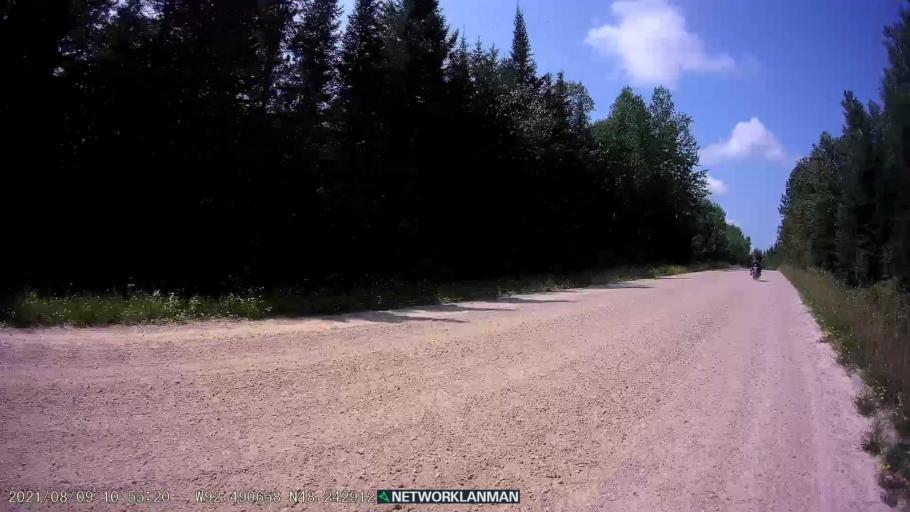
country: US
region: Minnesota
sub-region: Saint Louis County
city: Ely
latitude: 48.2430
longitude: -92.4911
